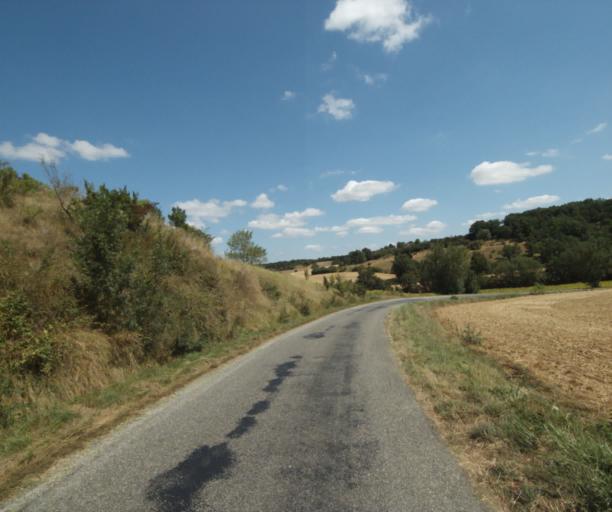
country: FR
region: Midi-Pyrenees
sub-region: Departement de la Haute-Garonne
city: Saint-Felix-Lauragais
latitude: 43.4691
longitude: 1.8462
